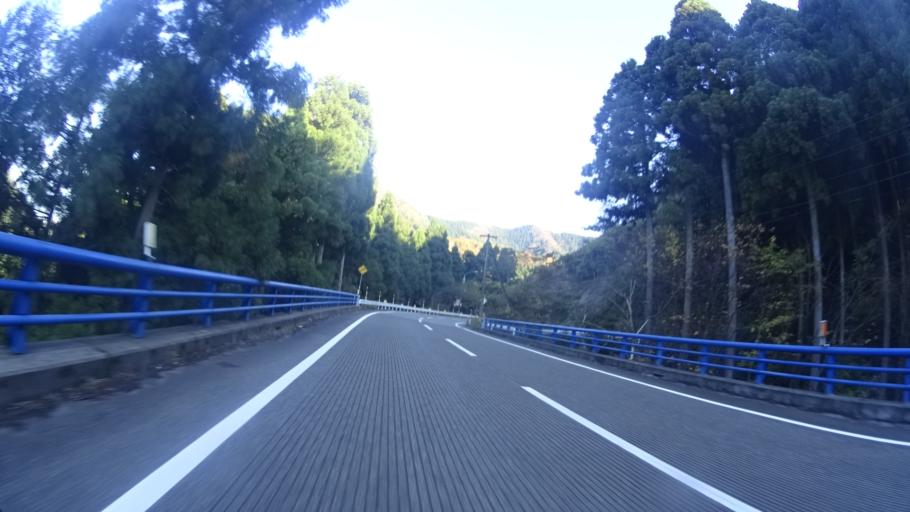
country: JP
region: Fukui
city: Maruoka
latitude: 36.1715
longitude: 136.3329
